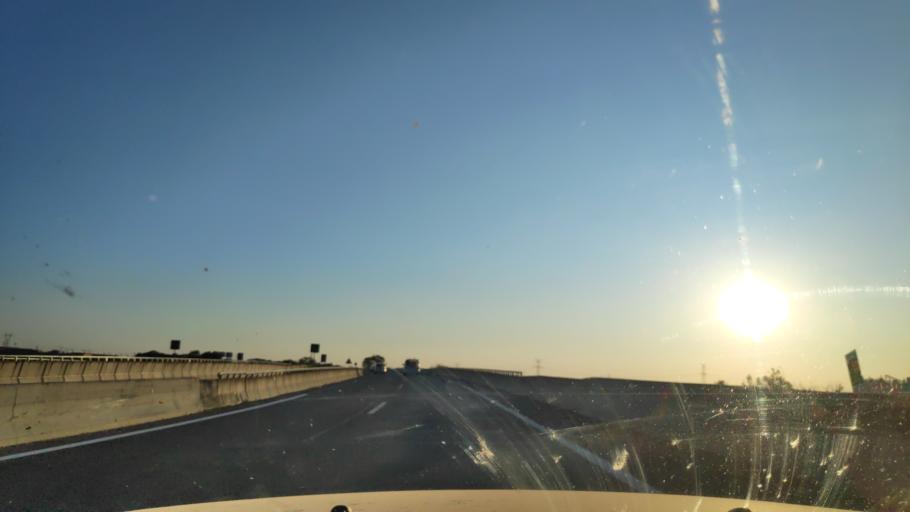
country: ES
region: Madrid
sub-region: Provincia de Madrid
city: Arganda
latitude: 40.2678
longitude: -3.3976
